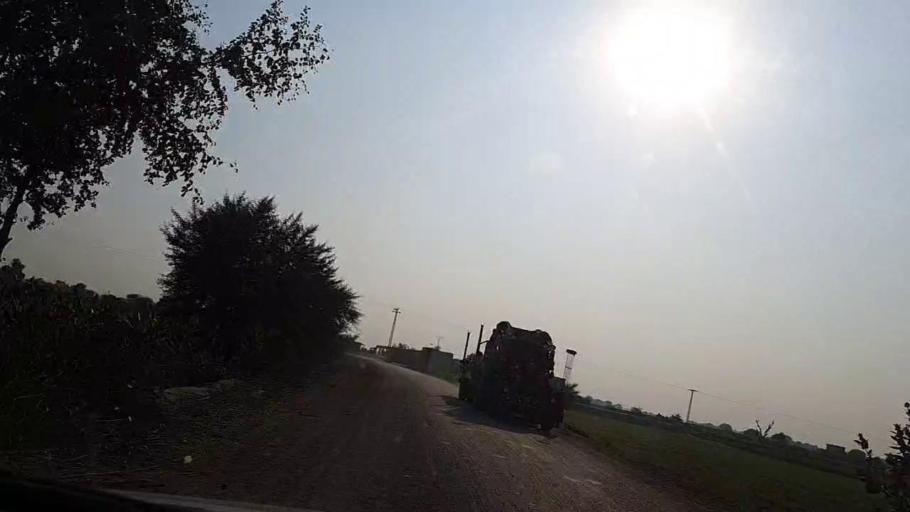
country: PK
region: Sindh
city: Sakrand
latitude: 26.0723
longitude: 68.2613
